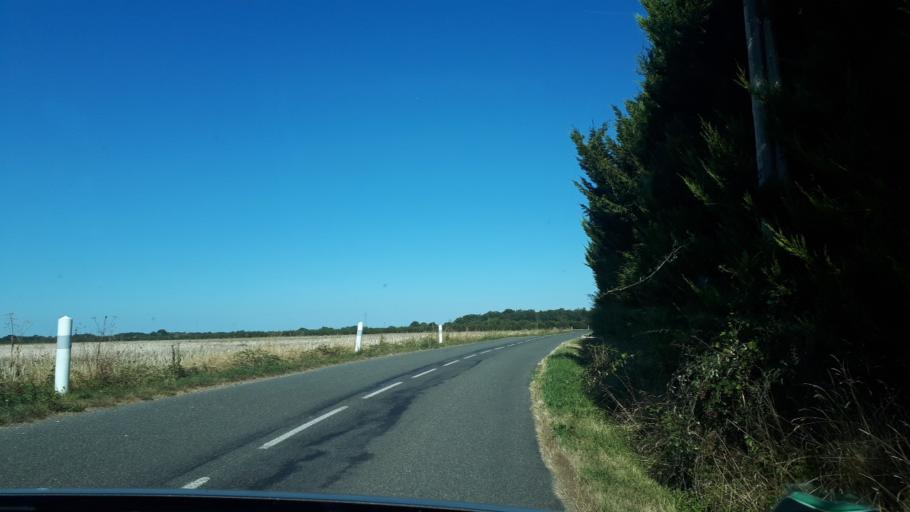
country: FR
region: Centre
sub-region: Departement du Loiret
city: Autry-le-Chatel
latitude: 47.6083
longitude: 2.5692
